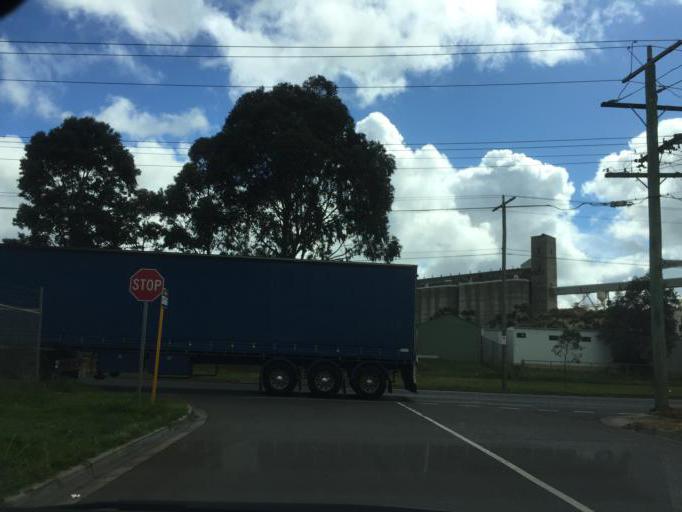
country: AU
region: Victoria
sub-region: Brimbank
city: Sunshine West
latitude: -37.7967
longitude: 144.8355
